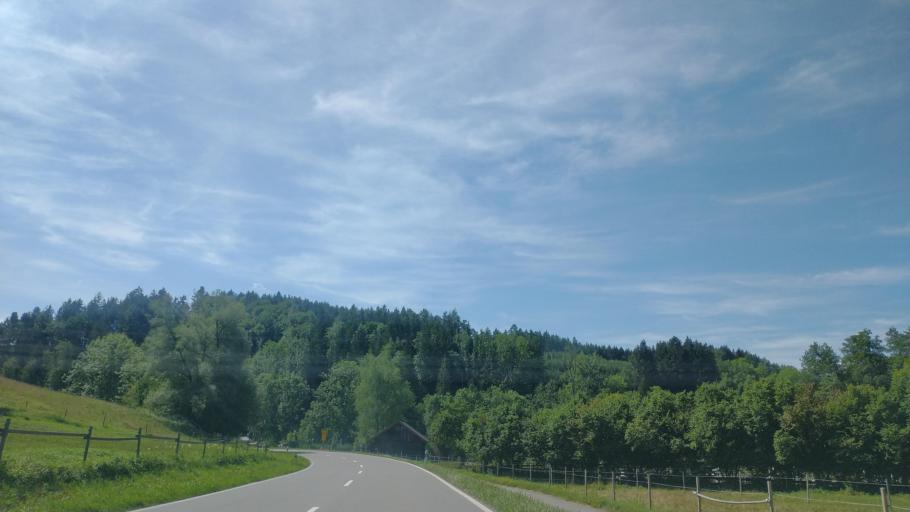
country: DE
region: Baden-Wuerttemberg
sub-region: Tuebingen Region
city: Neukirch
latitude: 47.6702
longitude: 9.7340
